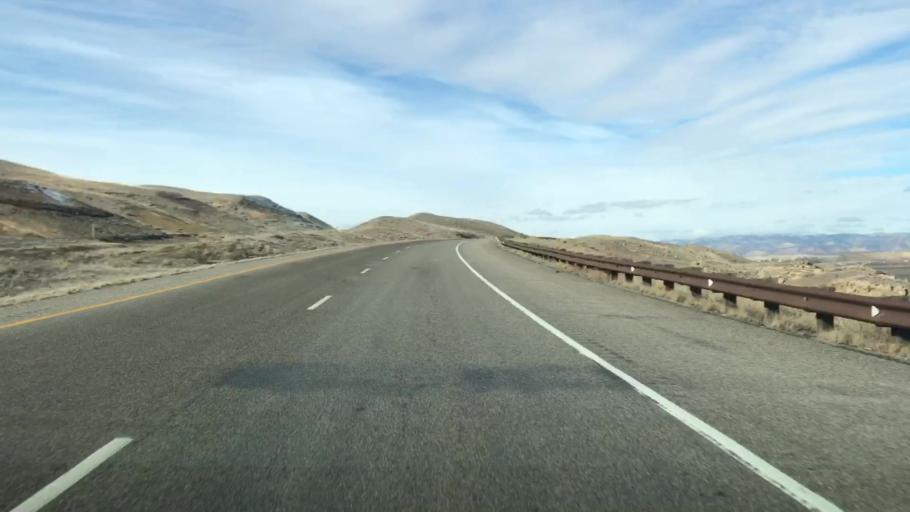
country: US
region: Colorado
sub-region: Mesa County
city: Loma
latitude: 39.2247
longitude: -108.8943
